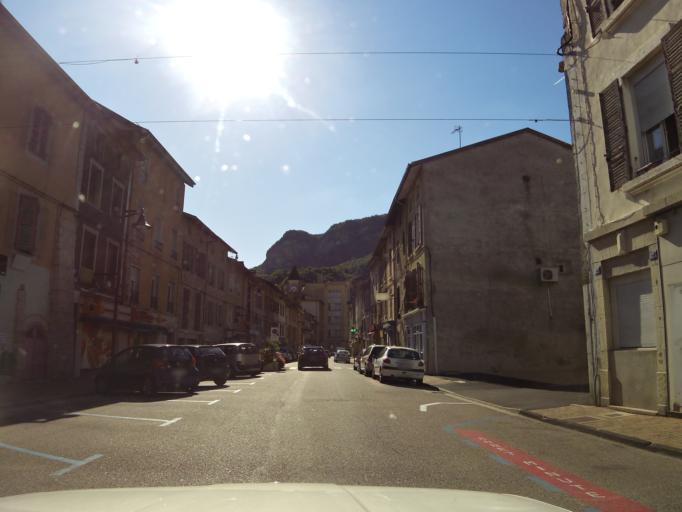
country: FR
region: Rhone-Alpes
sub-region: Departement de l'Ain
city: Saint-Rambert-en-Bugey
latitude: 45.9491
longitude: 5.4410
